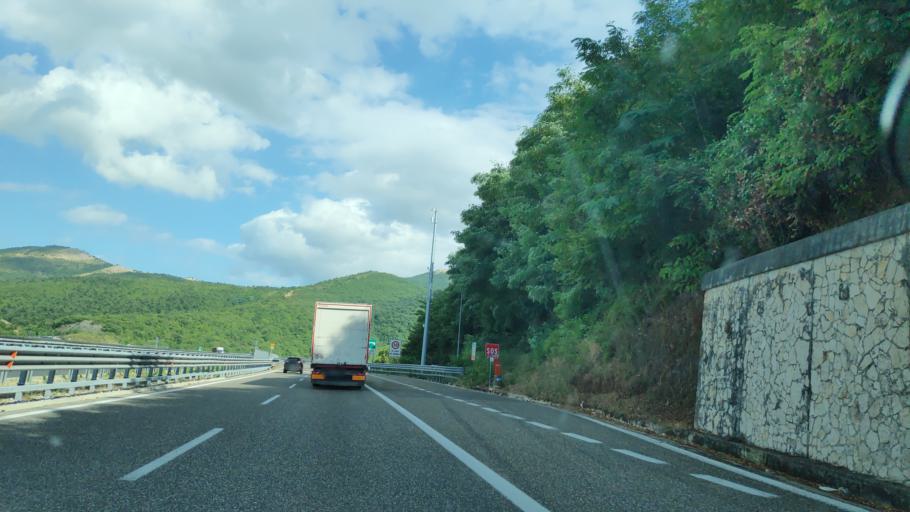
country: IT
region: Campania
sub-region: Provincia di Salerno
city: Pertosa
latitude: 40.5316
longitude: 15.4268
